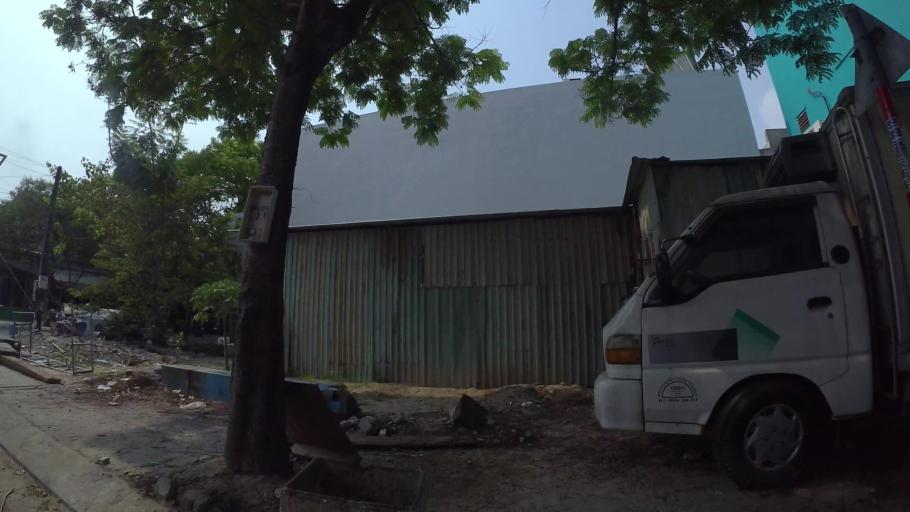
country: VN
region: Da Nang
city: Da Nang
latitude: 16.0920
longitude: 108.2363
